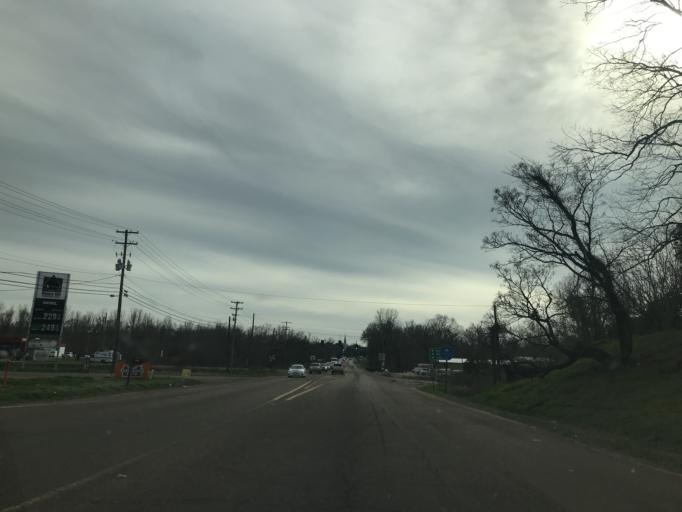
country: US
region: Mississippi
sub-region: Claiborne County
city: Port Gibson
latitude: 31.9694
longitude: -90.9788
